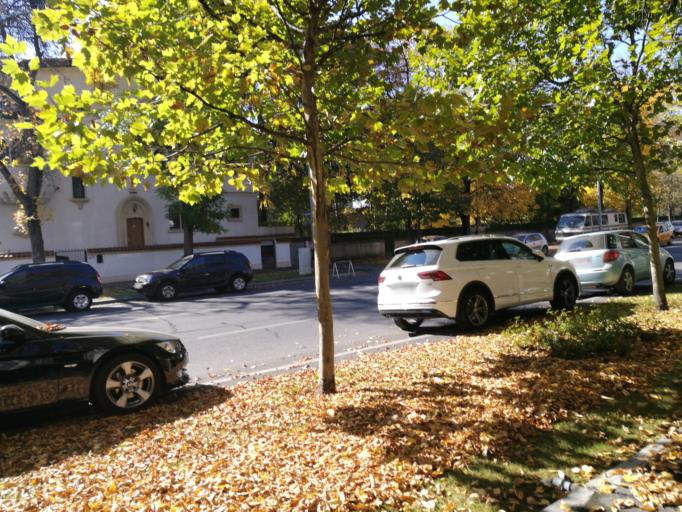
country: RO
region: Bucuresti
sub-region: Municipiul Bucuresti
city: Bucharest
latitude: 44.4702
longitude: 26.0922
